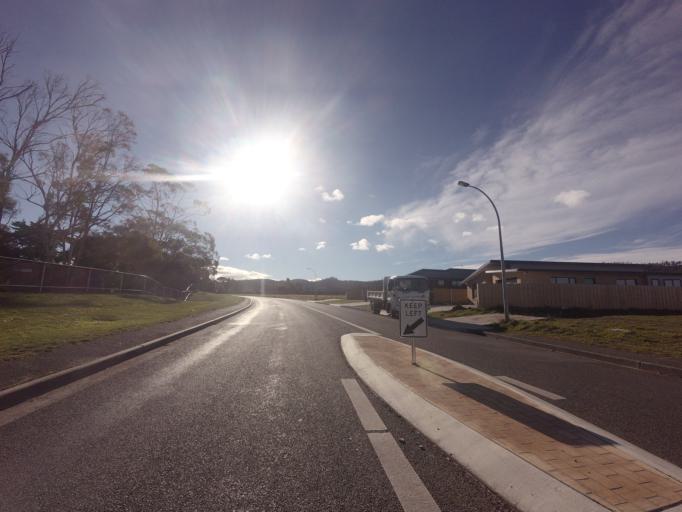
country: AU
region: Tasmania
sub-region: Clarence
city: Rokeby
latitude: -42.8977
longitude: 147.4469
